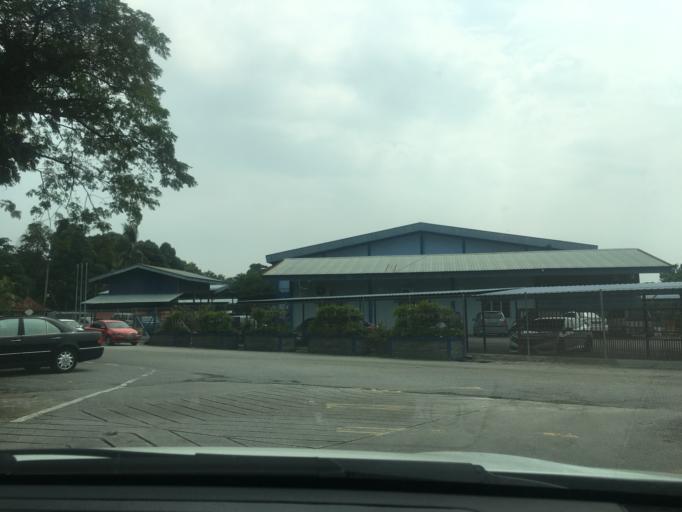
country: MY
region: Selangor
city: Klang
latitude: 3.0492
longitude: 101.4404
